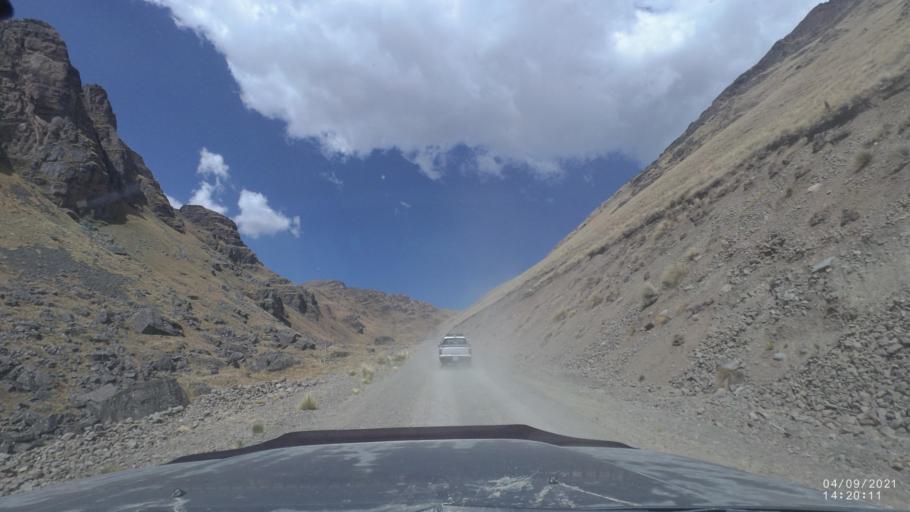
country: BO
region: Cochabamba
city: Sipe Sipe
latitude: -17.2345
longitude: -66.4214
